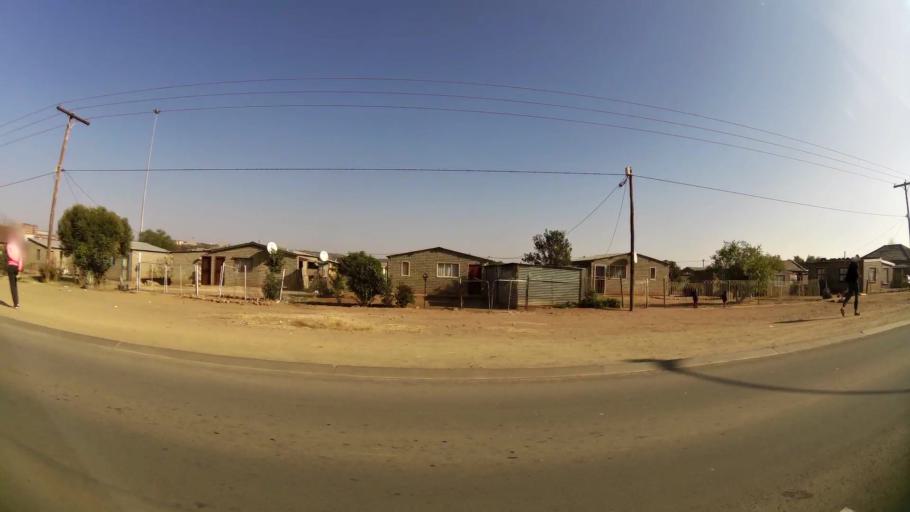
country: ZA
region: Orange Free State
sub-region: Mangaung Metropolitan Municipality
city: Bloemfontein
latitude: -29.1816
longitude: 26.2238
